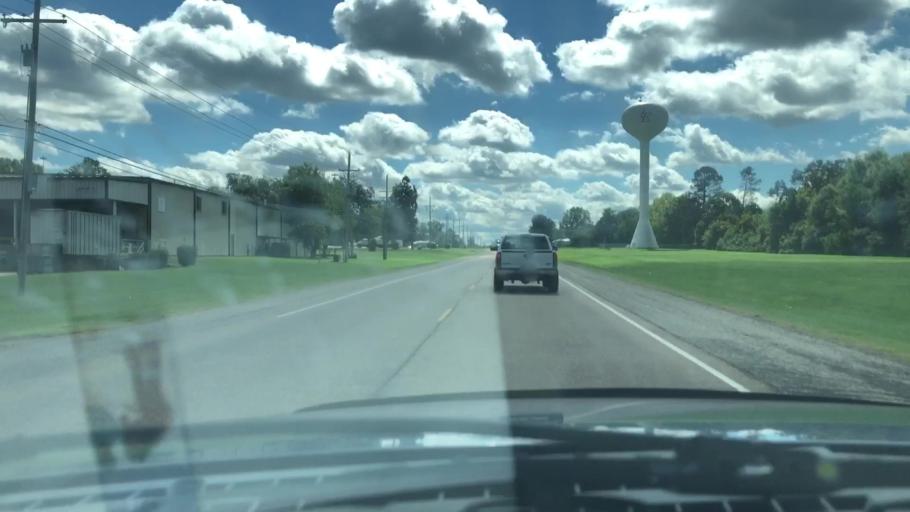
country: US
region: Texas
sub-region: Bowie County
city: Wake Village
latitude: 33.3800
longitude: -94.0921
